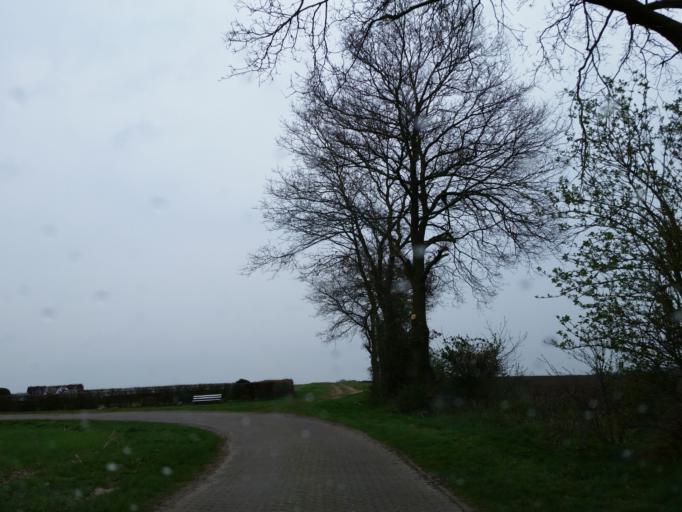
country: DE
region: Lower Saxony
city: Alfstedt
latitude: 53.5717
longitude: 9.0117
